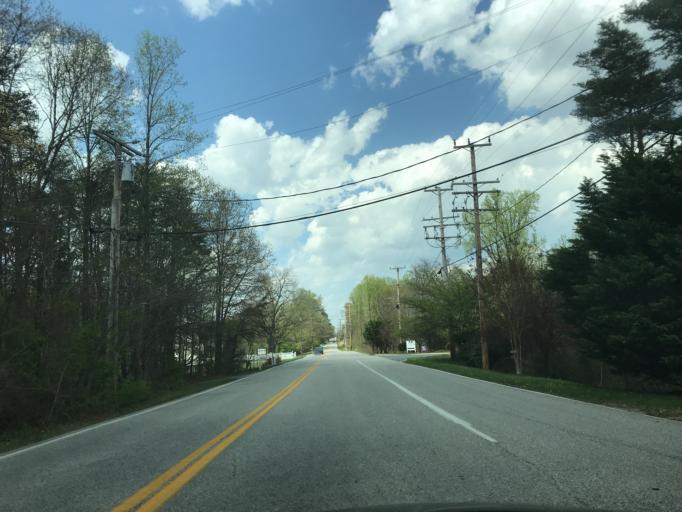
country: US
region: Maryland
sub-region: Anne Arundel County
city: Severn
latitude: 39.1469
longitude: -76.6703
